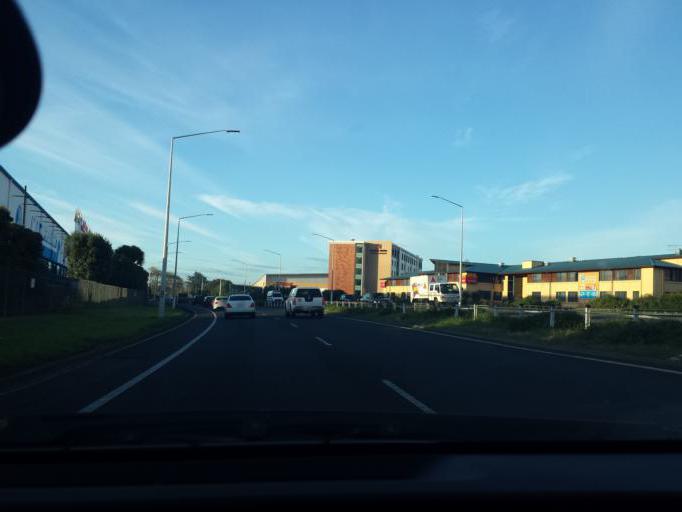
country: NZ
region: Auckland
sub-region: Auckland
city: Mangere
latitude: -36.9827
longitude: 174.7845
